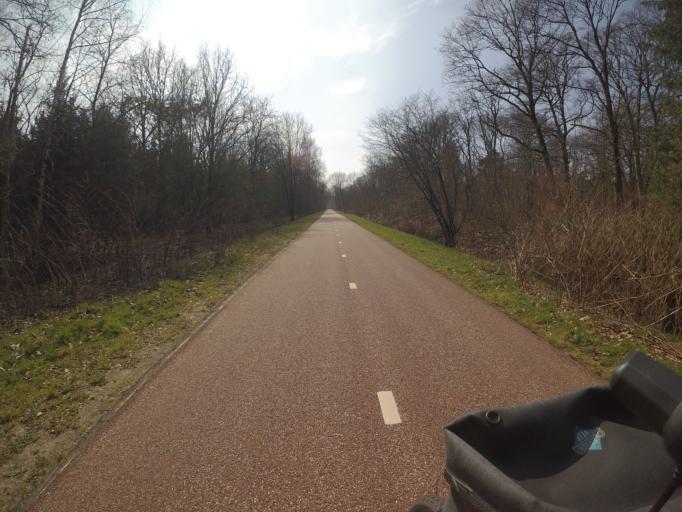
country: NL
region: North Brabant
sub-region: Gemeente Goirle
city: Goirle
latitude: 51.5582
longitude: 5.0220
